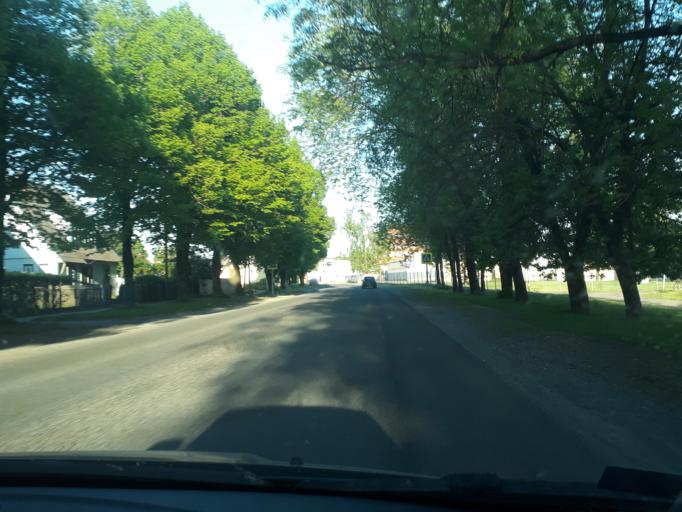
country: EE
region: Paernumaa
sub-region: Paernu linn
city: Parnu
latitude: 58.3896
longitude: 24.5240
